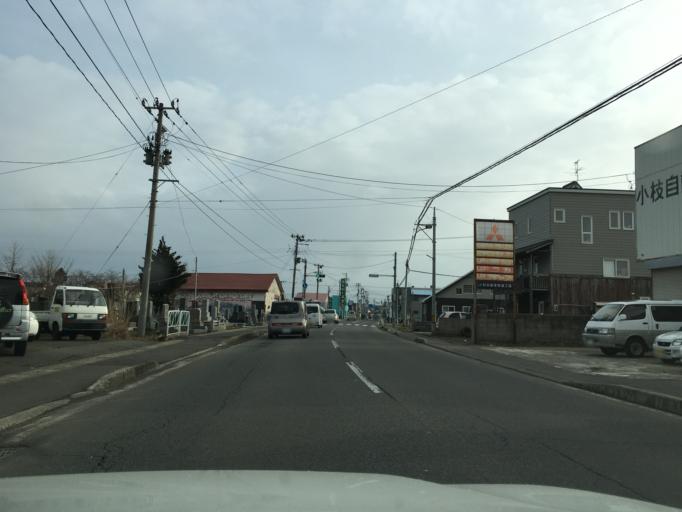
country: JP
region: Aomori
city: Namioka
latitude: 40.7148
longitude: 140.5910
